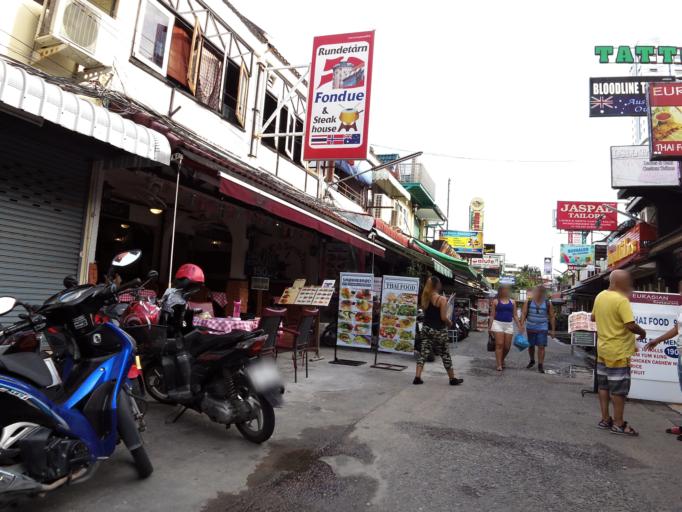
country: TH
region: Phuket
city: Patong
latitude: 7.8928
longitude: 98.2966
